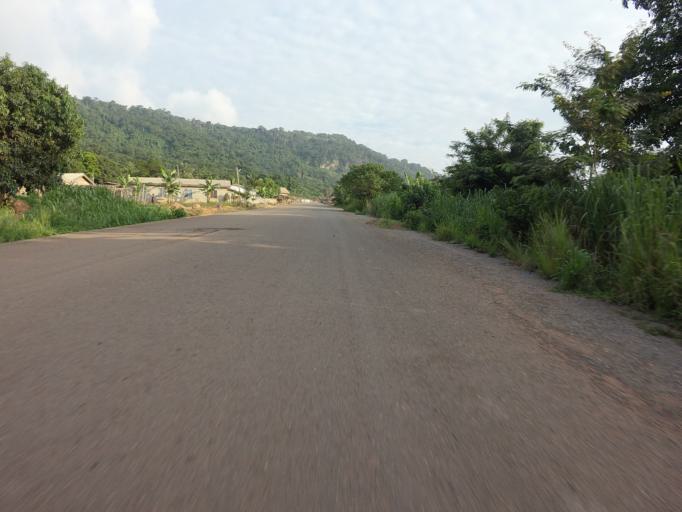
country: TG
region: Plateaux
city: Kpalime
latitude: 6.9225
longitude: 0.4611
